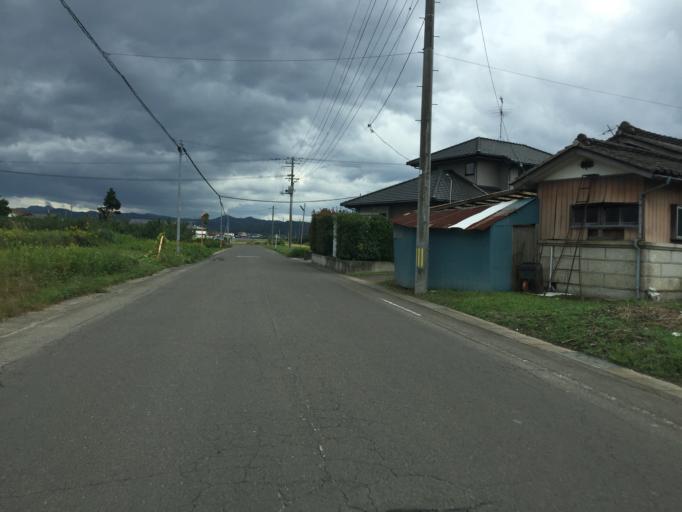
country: JP
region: Fukushima
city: Hobaramachi
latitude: 37.8344
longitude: 140.5487
